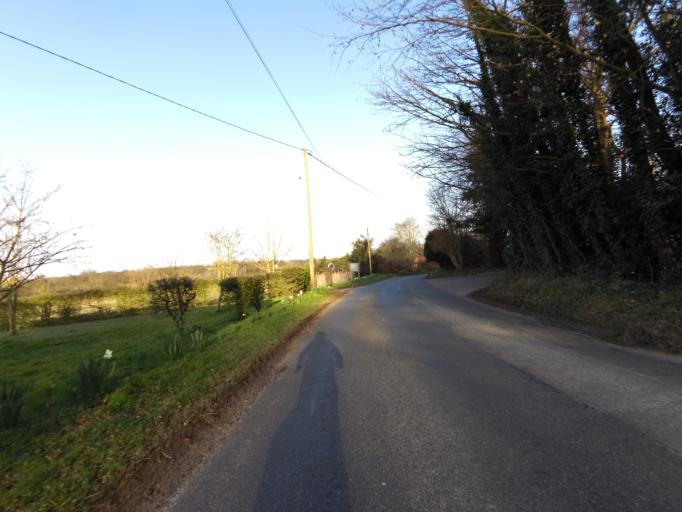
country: GB
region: England
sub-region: Suffolk
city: Kesgrave
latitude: 52.0793
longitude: 1.2776
